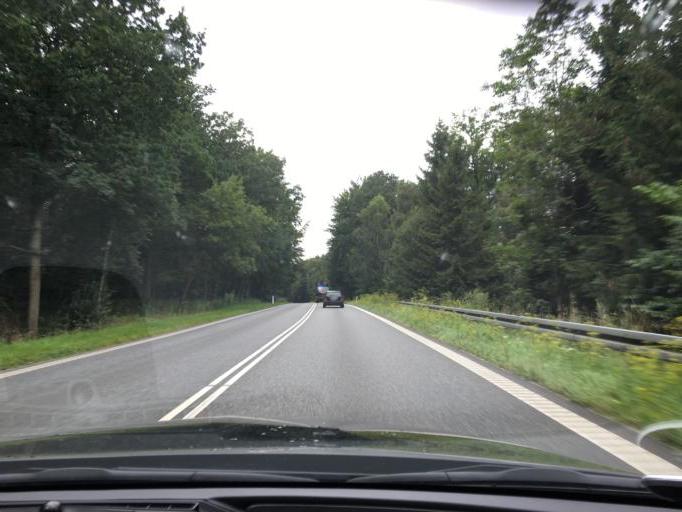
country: DK
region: Capital Region
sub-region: Hillerod Kommune
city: Nodebo
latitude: 55.9478
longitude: 12.3396
